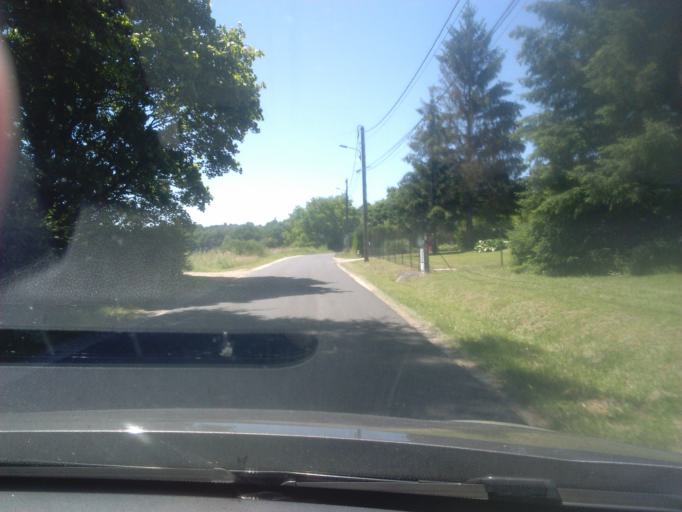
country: FR
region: Centre
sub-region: Departement du Loir-et-Cher
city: Saint-Sulpice-de-Pommeray
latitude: 47.6047
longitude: 1.2296
